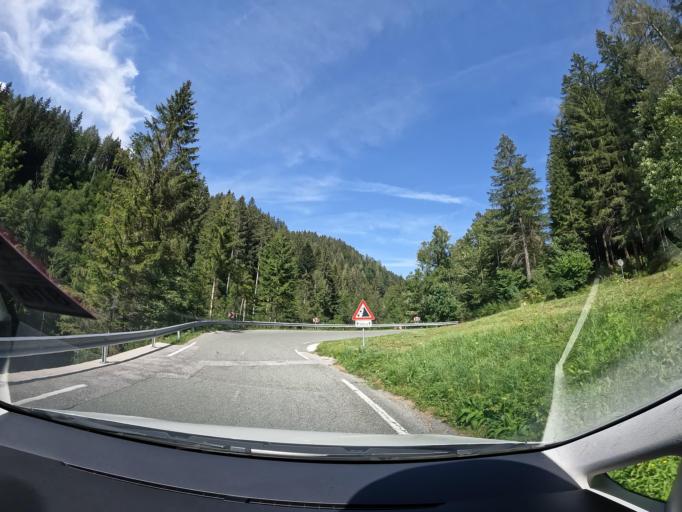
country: SI
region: Jesenice
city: Koroska Bela
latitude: 46.5000
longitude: 14.0994
